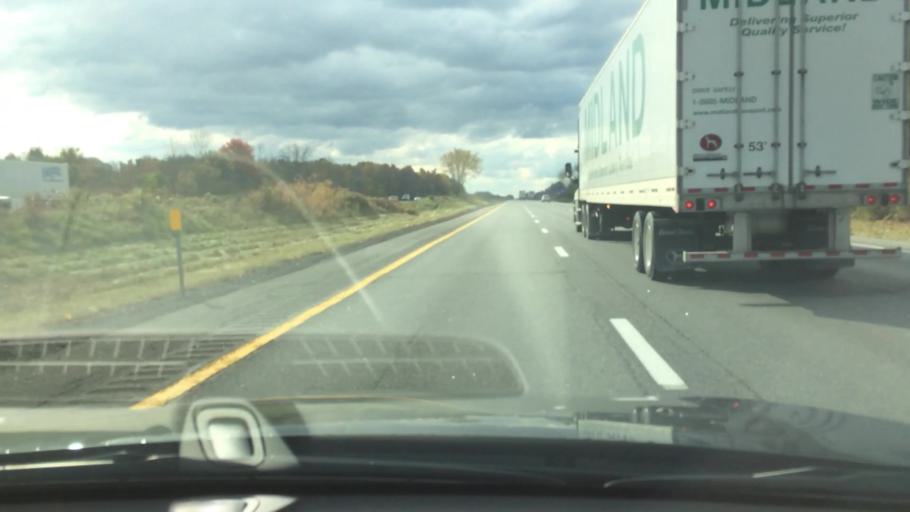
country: US
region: New York
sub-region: Saratoga County
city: Ballston Spa
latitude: 42.9832
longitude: -73.8033
